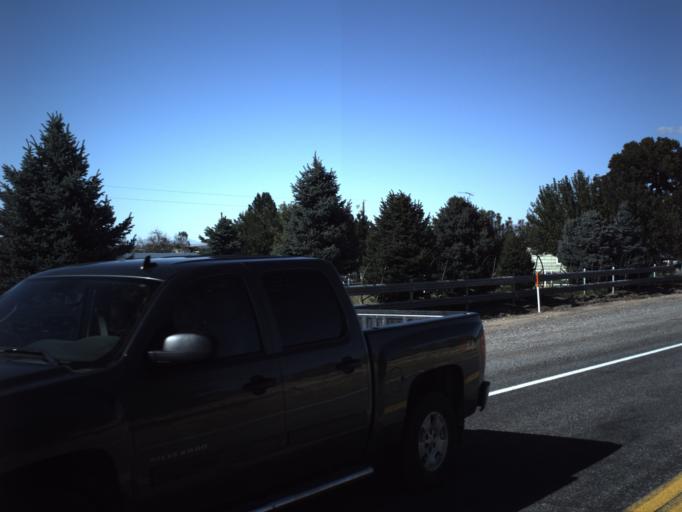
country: US
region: Utah
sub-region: Millard County
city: Fillmore
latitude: 39.0898
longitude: -112.2725
